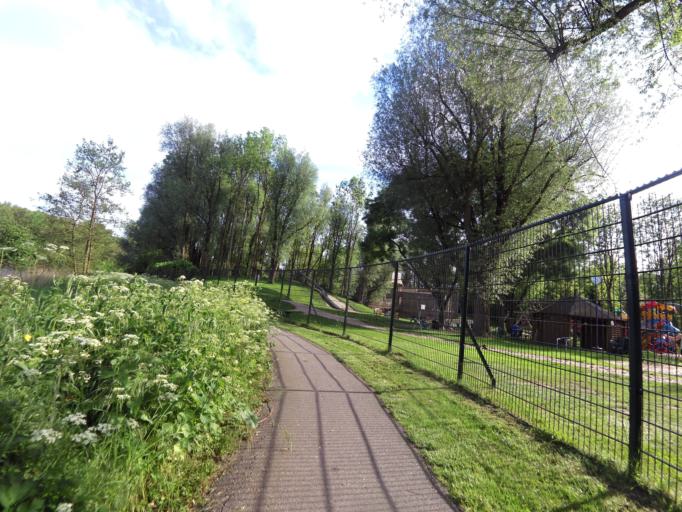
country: NL
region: South Holland
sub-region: Gemeente Zoetermeer
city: Zoetermeer
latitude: 52.0609
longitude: 4.4533
